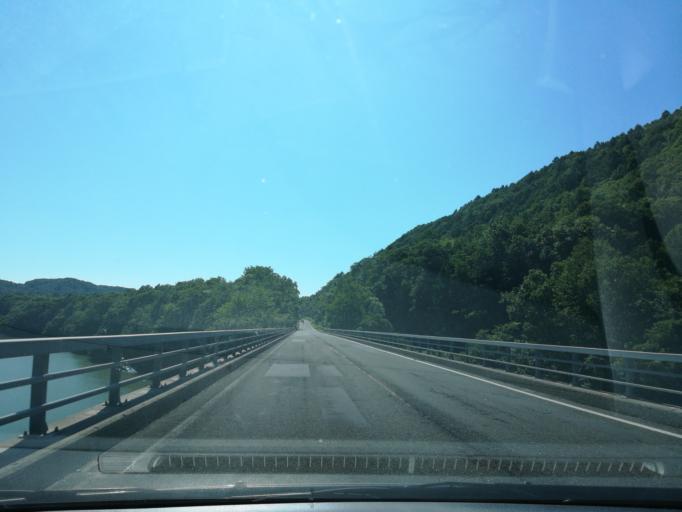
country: JP
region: Hokkaido
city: Chitose
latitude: 42.9102
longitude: 141.9438
